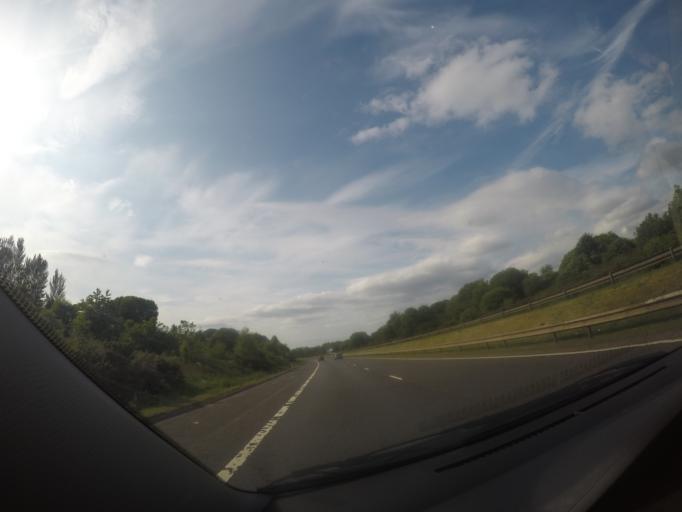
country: GB
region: Scotland
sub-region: South Lanarkshire
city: Larkhall
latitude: 55.7389
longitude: -3.9519
